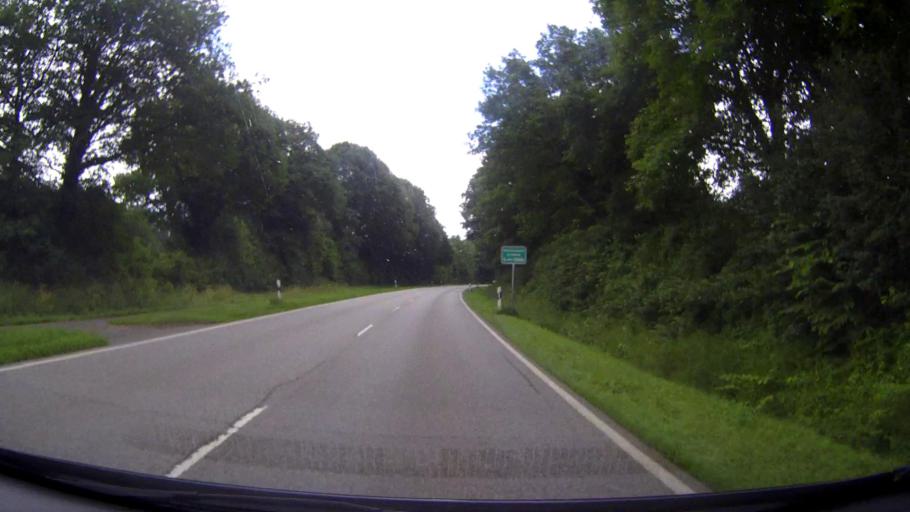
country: DE
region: Schleswig-Holstein
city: Meezen
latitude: 54.0750
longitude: 9.7246
